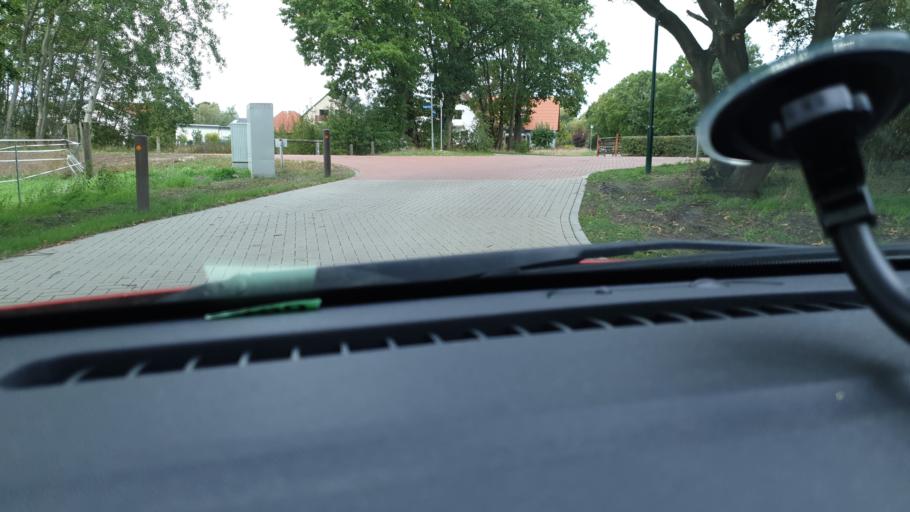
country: DE
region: Lower Saxony
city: Langlingen
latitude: 52.5549
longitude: 10.2790
